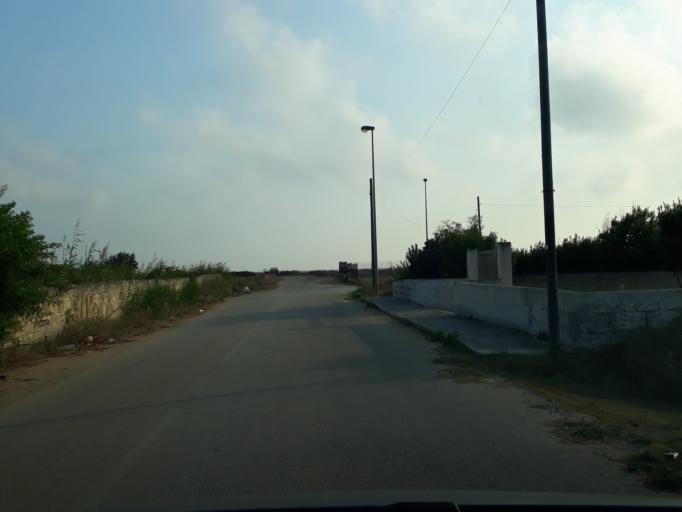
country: IT
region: Apulia
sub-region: Provincia di Brindisi
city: Carovigno
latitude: 40.7514
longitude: 17.7167
